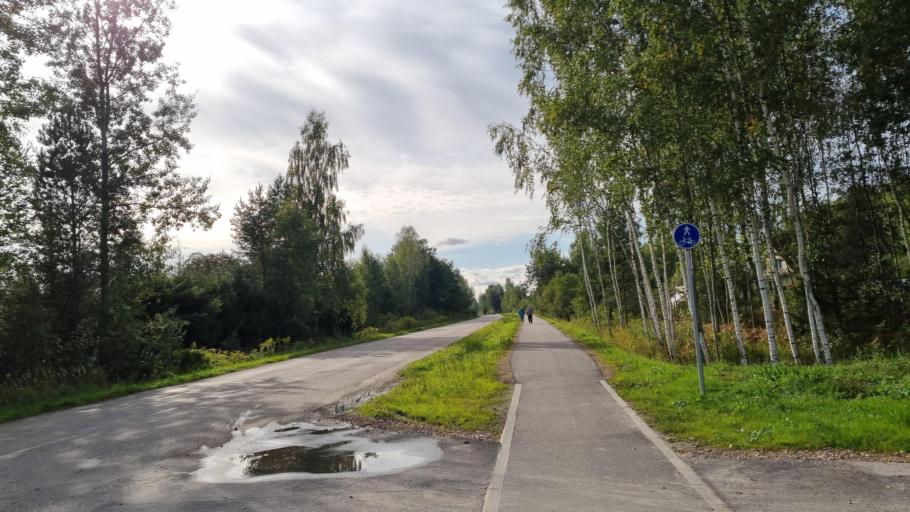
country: LV
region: Olaine
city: Olaine
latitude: 56.6994
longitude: 24.0670
